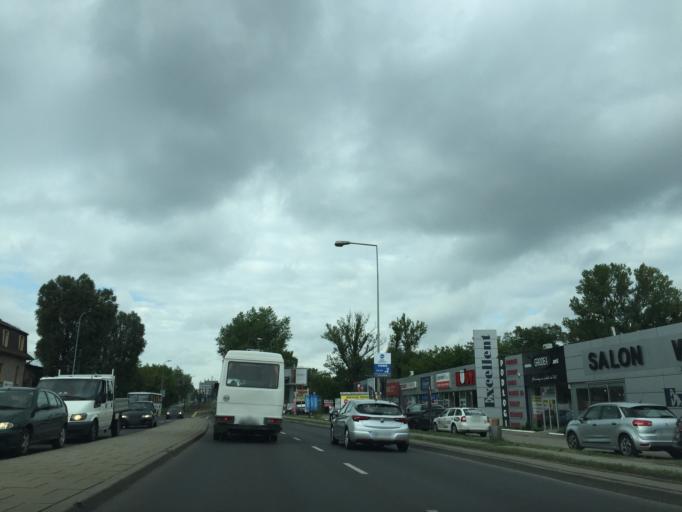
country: PL
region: Lesser Poland Voivodeship
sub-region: Krakow
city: Krakow
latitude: 50.0192
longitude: 19.9315
